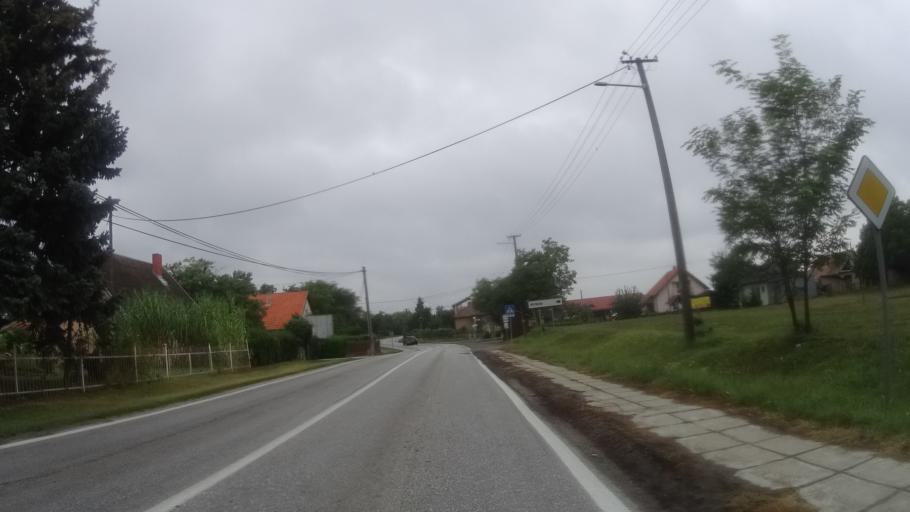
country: HU
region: Komarom-Esztergom
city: Neszmely
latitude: 47.7488
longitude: 18.3773
